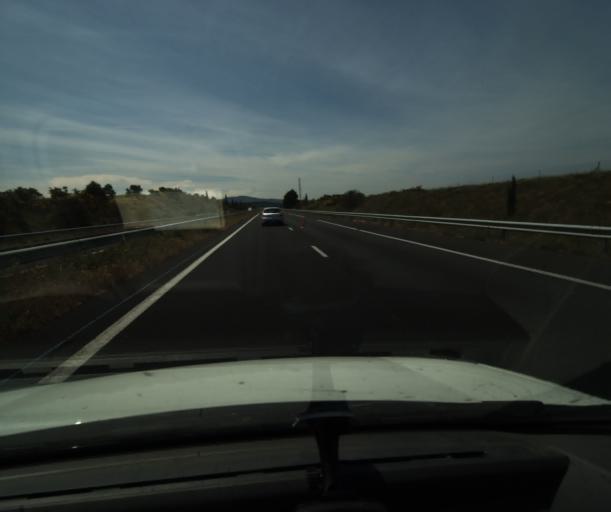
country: FR
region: Languedoc-Roussillon
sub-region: Departement de l'Aude
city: Ornaisons
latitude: 43.1710
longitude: 2.7957
